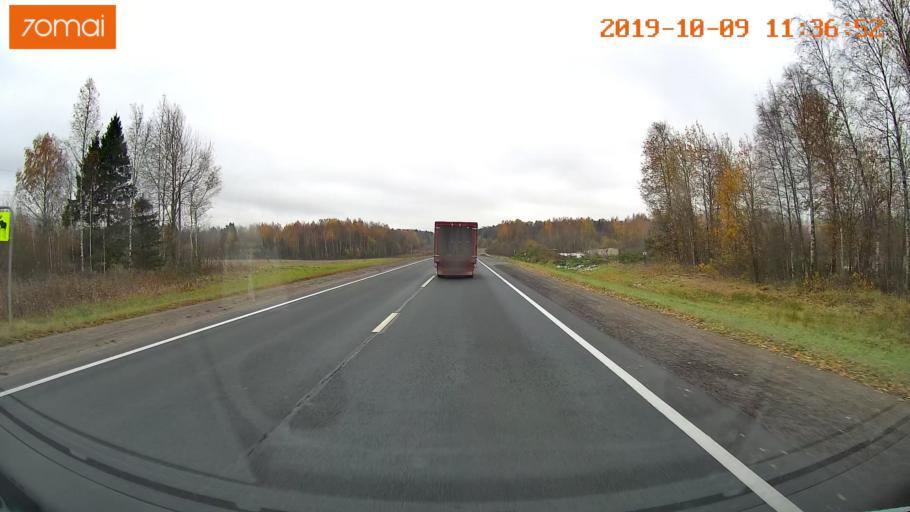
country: RU
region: Vologda
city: Gryazovets
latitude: 58.9852
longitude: 40.1417
